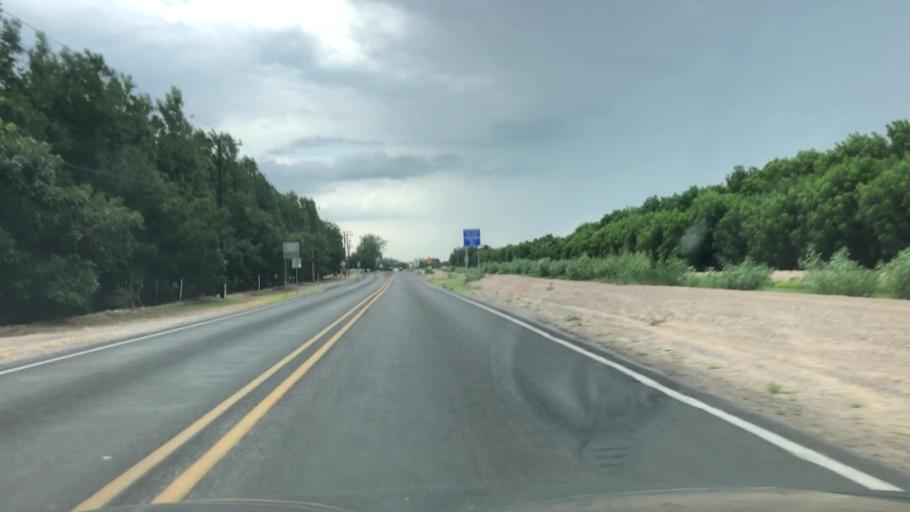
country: US
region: New Mexico
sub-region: Dona Ana County
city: La Union
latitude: 31.9942
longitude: -106.6532
